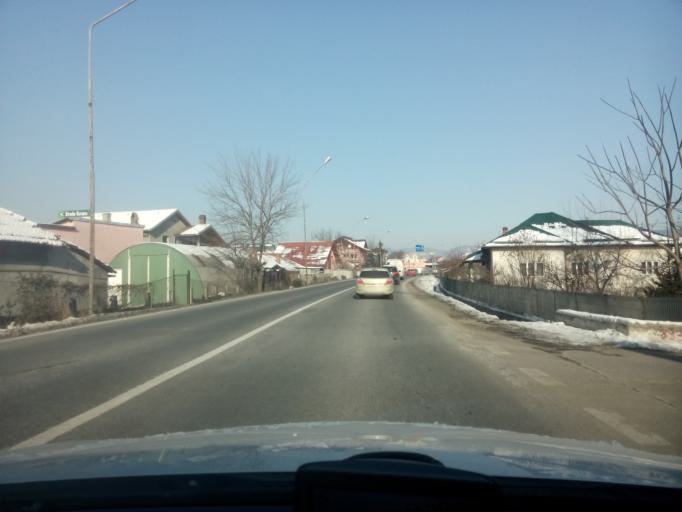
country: RO
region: Valcea
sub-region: Municipiul Ramnicu Valcea
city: Goranu
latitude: 45.1009
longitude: 24.3825
